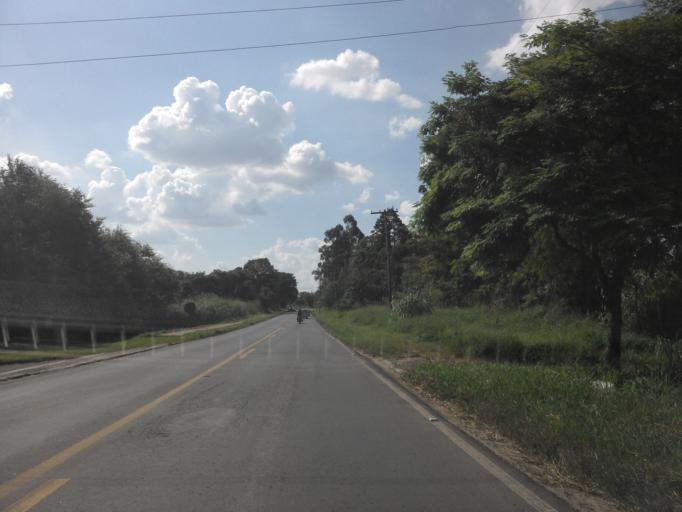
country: BR
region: Sao Paulo
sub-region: Valinhos
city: Valinhos
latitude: -23.0018
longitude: -47.0027
